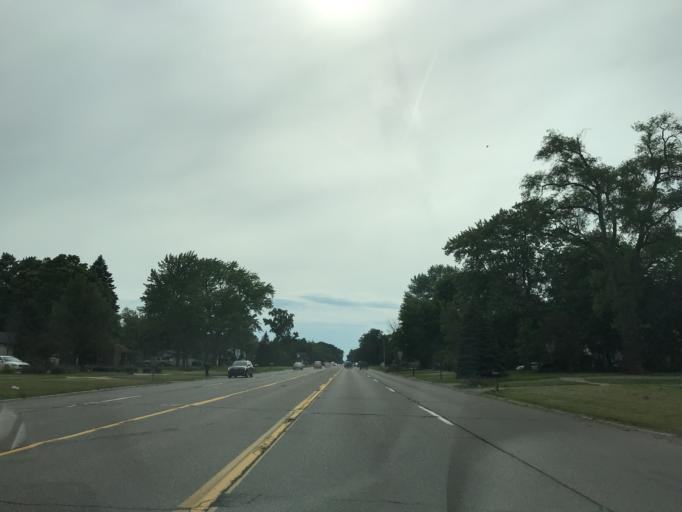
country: US
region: Michigan
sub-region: Wayne County
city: Livonia
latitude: 42.4125
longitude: -83.3406
